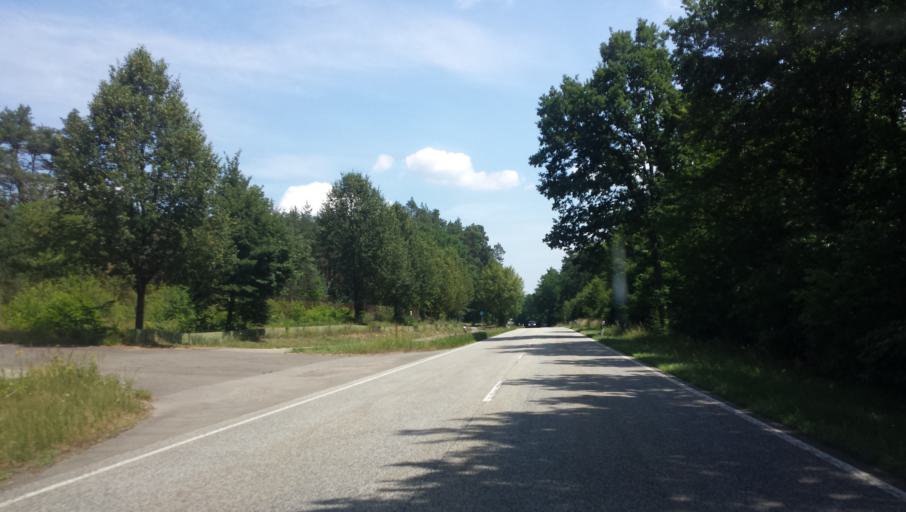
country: DE
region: Rheinland-Pfalz
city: Mehlingen
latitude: 49.4690
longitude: 7.8489
